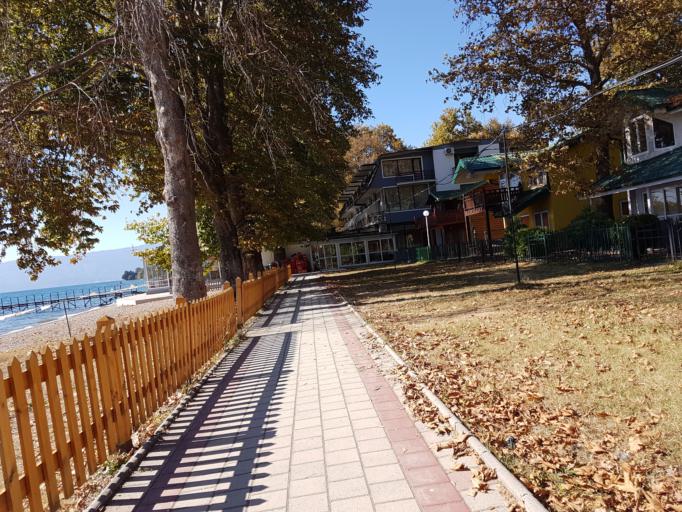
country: MK
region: Ohrid
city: Ohrid
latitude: 41.1187
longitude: 20.7851
